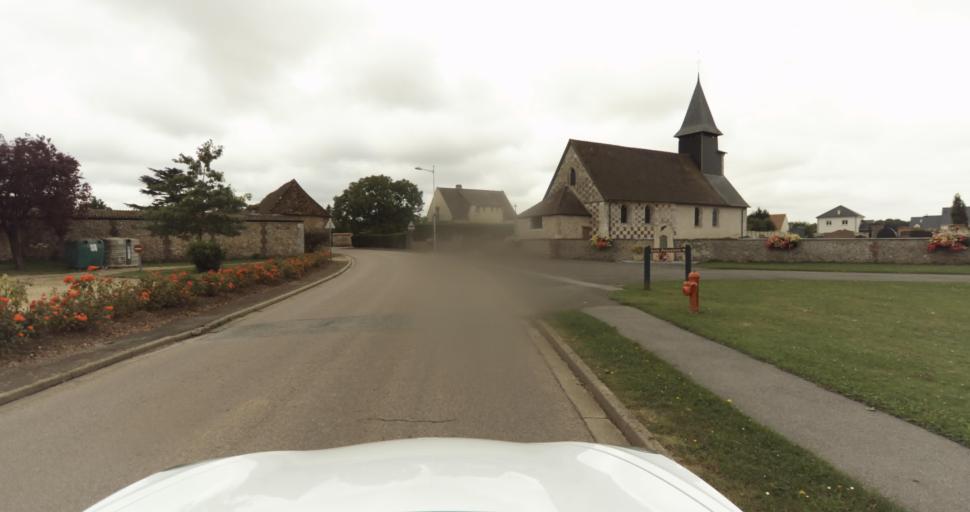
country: FR
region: Haute-Normandie
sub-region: Departement de l'Eure
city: Aviron
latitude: 49.0526
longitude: 1.0860
